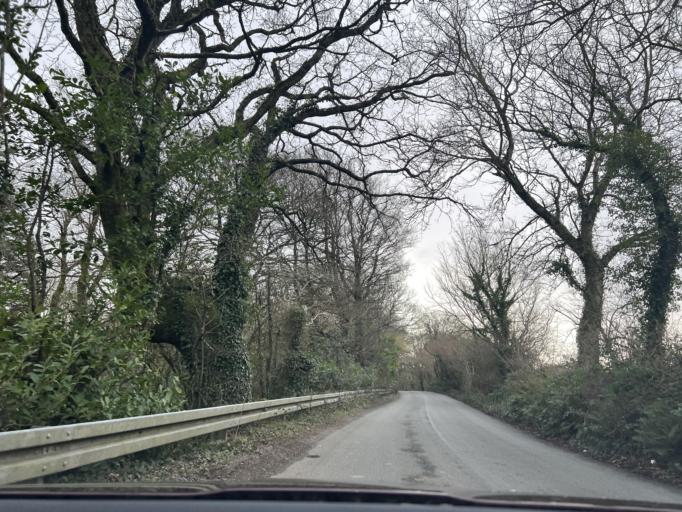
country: IE
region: Leinster
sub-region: Loch Garman
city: Castlebridge
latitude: 52.3808
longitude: -6.5394
